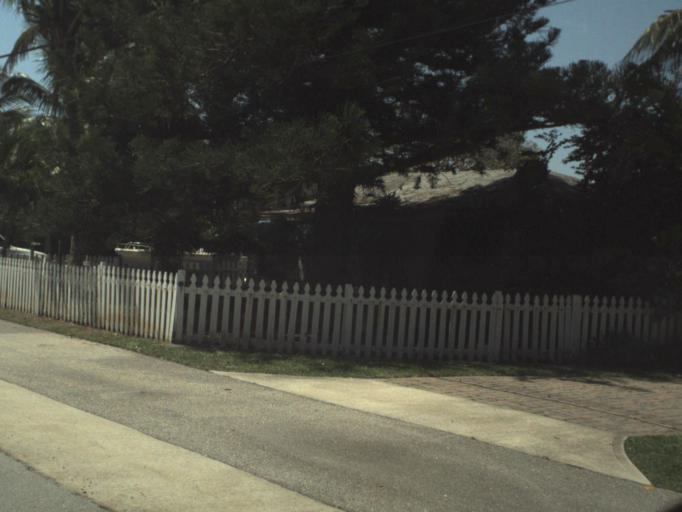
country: US
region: Florida
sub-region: Brevard County
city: Malabar
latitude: 27.9846
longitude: -80.5171
